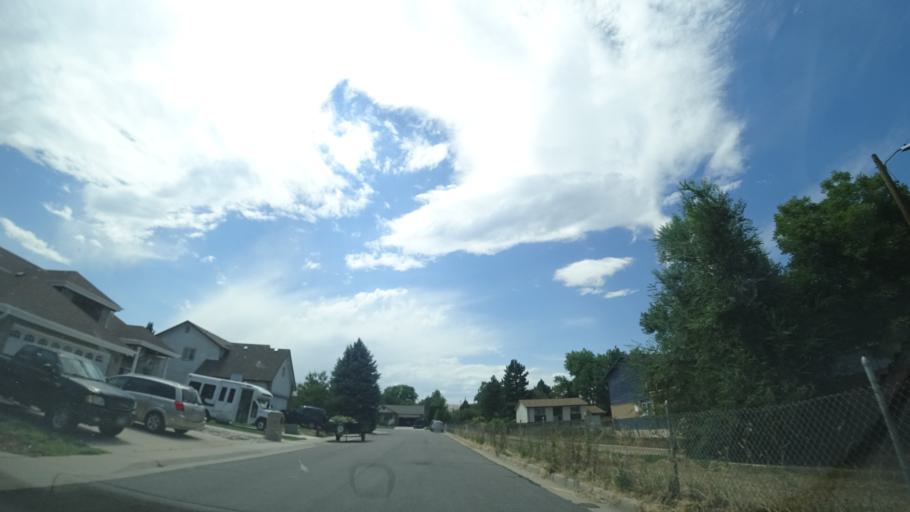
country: US
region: Colorado
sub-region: Jefferson County
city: Lakewood
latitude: 39.6957
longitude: -105.1008
